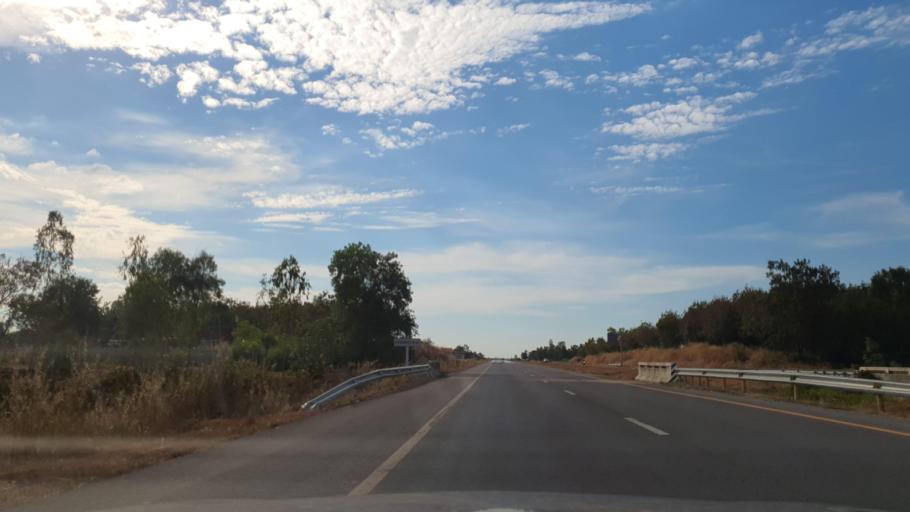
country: TH
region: Roi Et
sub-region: Amphoe Pho Chai
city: Pho Chai
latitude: 16.4137
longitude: 103.7881
